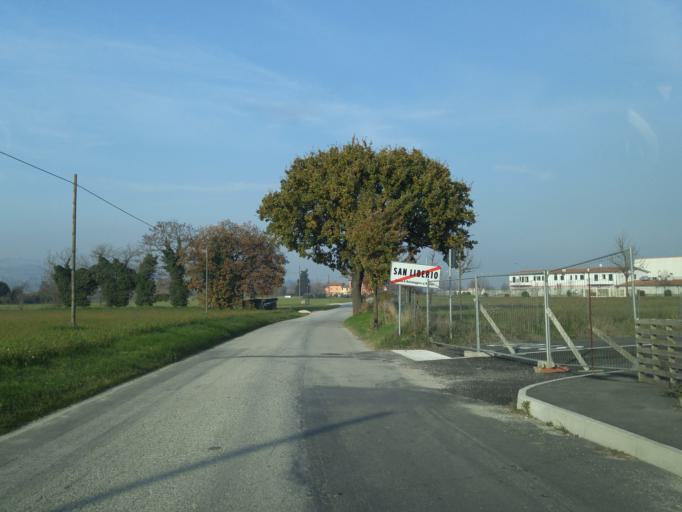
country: IT
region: The Marches
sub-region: Provincia di Pesaro e Urbino
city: Villanova
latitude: 43.7318
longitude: 12.9216
